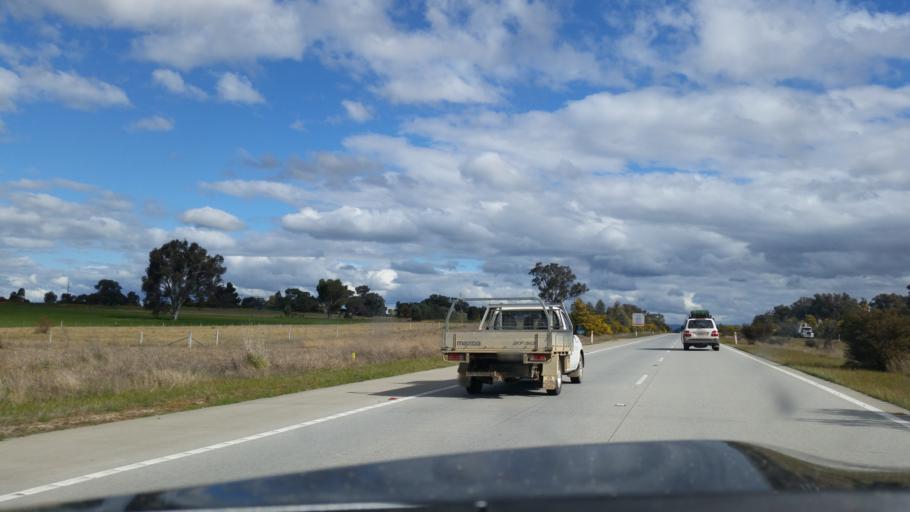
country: AU
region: New South Wales
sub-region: Albury Municipality
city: Lavington
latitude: -36.0067
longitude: 146.9901
